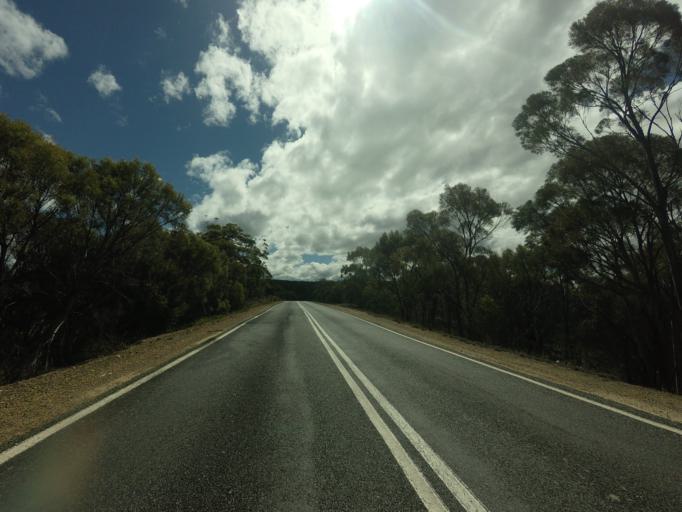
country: AU
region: Tasmania
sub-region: Break O'Day
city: St Helens
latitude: -42.0165
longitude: 147.9840
